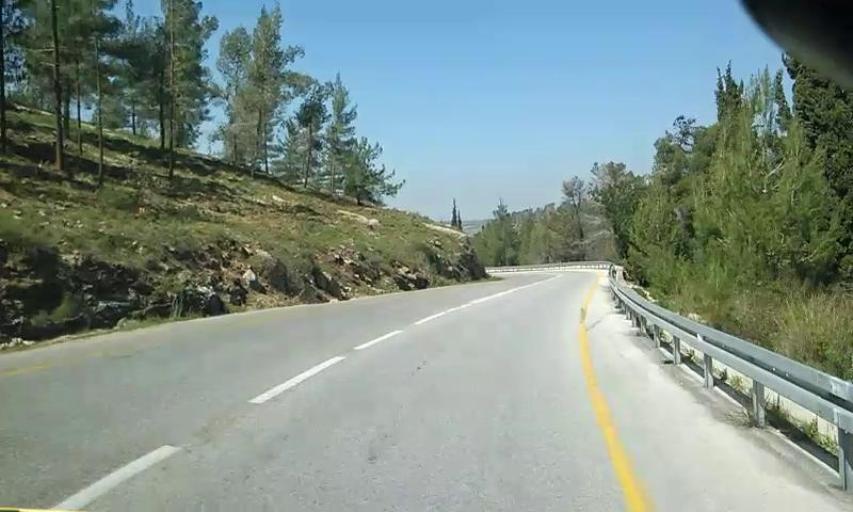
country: PS
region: West Bank
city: Nahhalin
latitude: 31.6731
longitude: 35.1041
